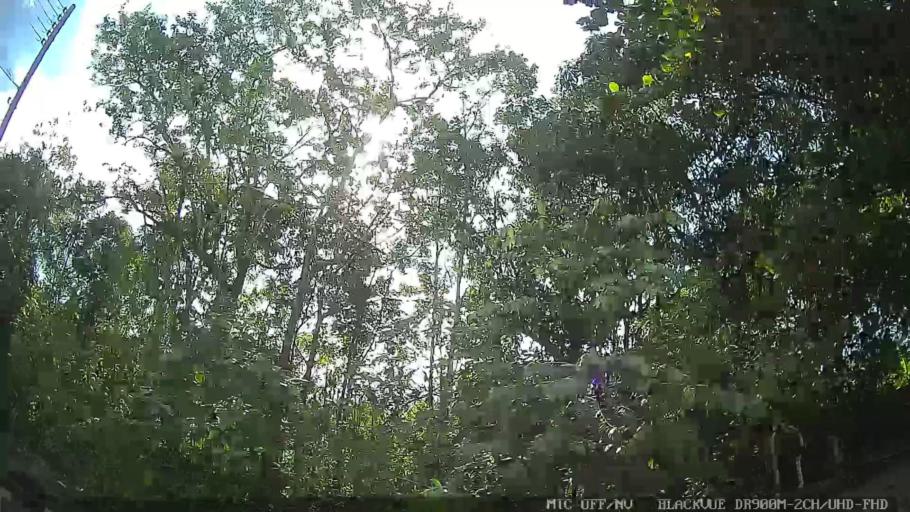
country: BR
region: Sao Paulo
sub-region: Guaruja
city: Guaruja
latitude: -23.9618
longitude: -46.2568
